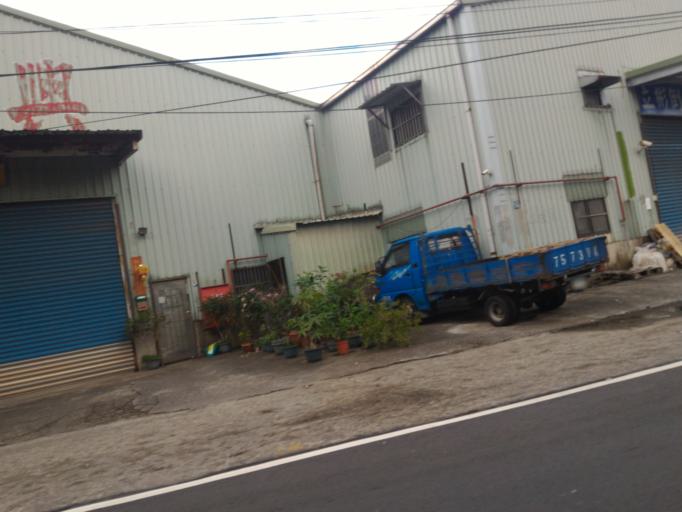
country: TW
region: Taiwan
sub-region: Taoyuan
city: Taoyuan
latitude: 24.9507
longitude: 121.3921
